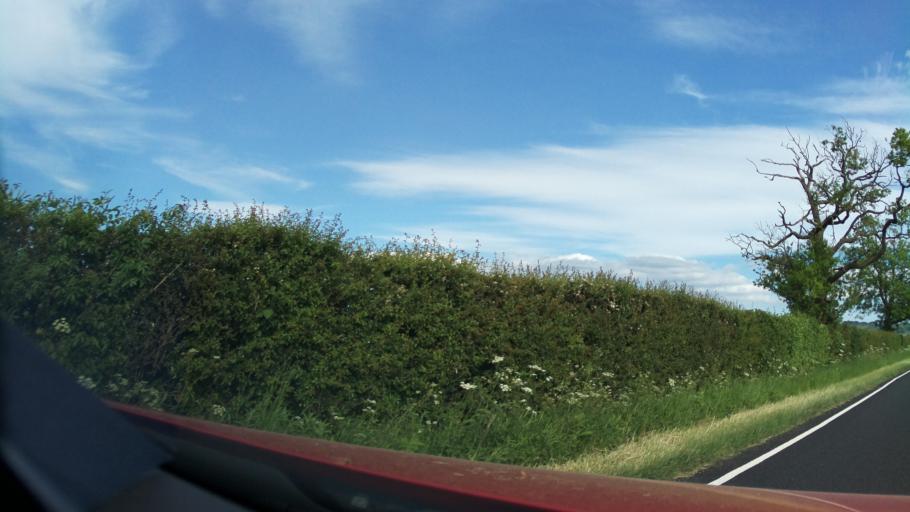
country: GB
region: England
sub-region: Worcestershire
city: Broadway
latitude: 52.0809
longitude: -1.8491
